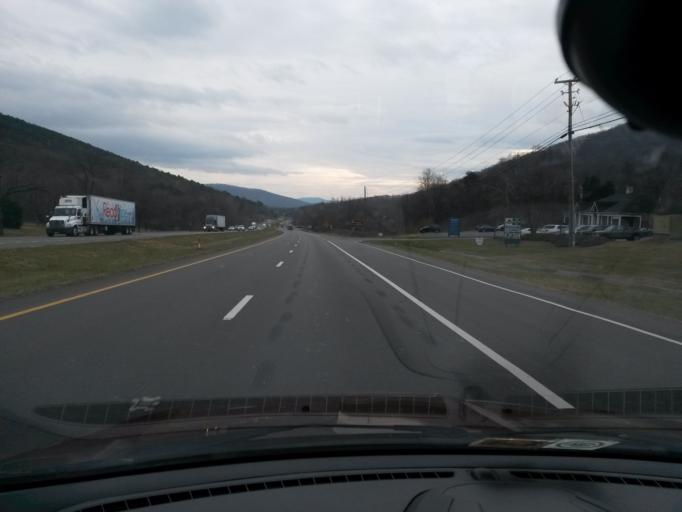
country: US
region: Virginia
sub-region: Botetourt County
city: Cloverdale
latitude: 37.3565
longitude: -79.8850
